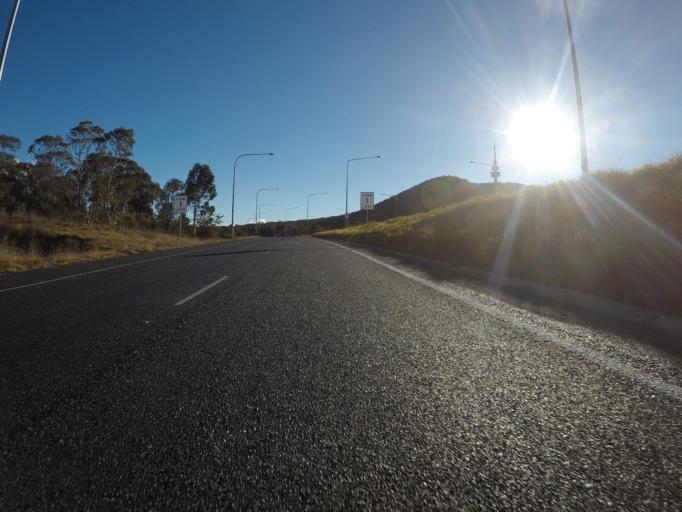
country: AU
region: Australian Capital Territory
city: Acton
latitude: -35.2835
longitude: 149.0853
